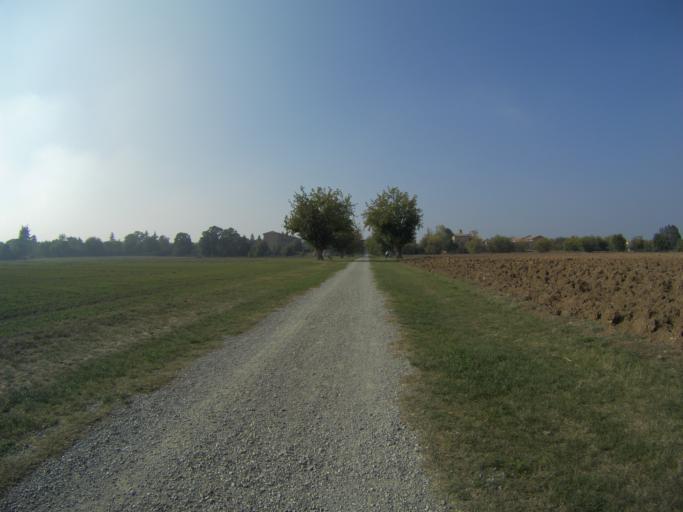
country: IT
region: Emilia-Romagna
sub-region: Provincia di Reggio Emilia
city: Forche
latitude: 44.6599
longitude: 10.5957
